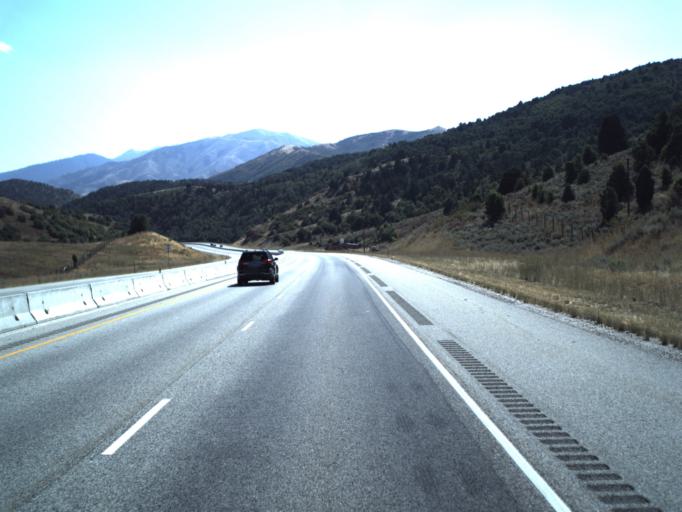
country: US
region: Utah
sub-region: Box Elder County
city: Brigham City
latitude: 41.5415
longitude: -111.9572
